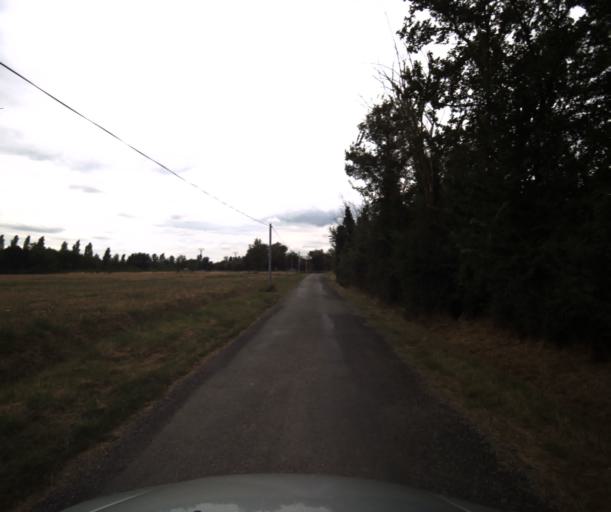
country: FR
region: Midi-Pyrenees
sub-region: Departement de la Haute-Garonne
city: Le Fauga
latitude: 43.4401
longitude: 1.3077
